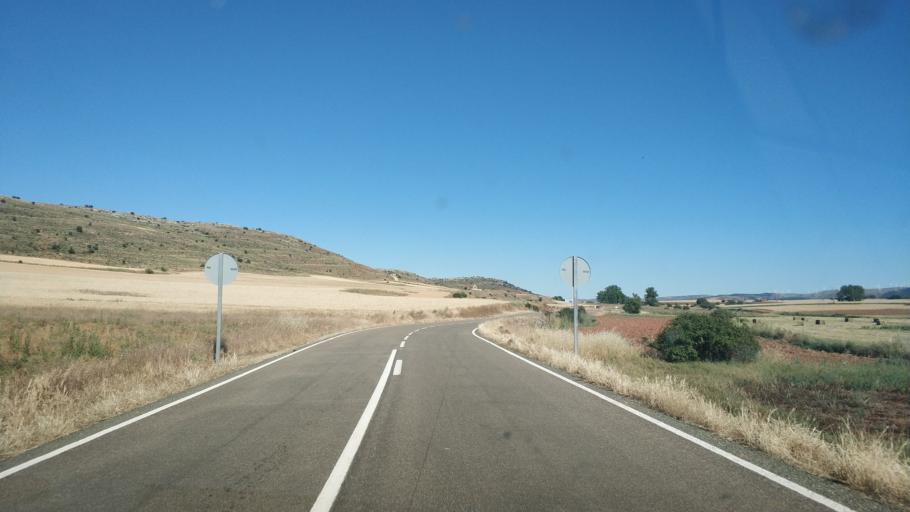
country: ES
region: Castille and Leon
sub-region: Provincia de Soria
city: Montejo de Tiermes
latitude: 41.3658
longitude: -3.1924
